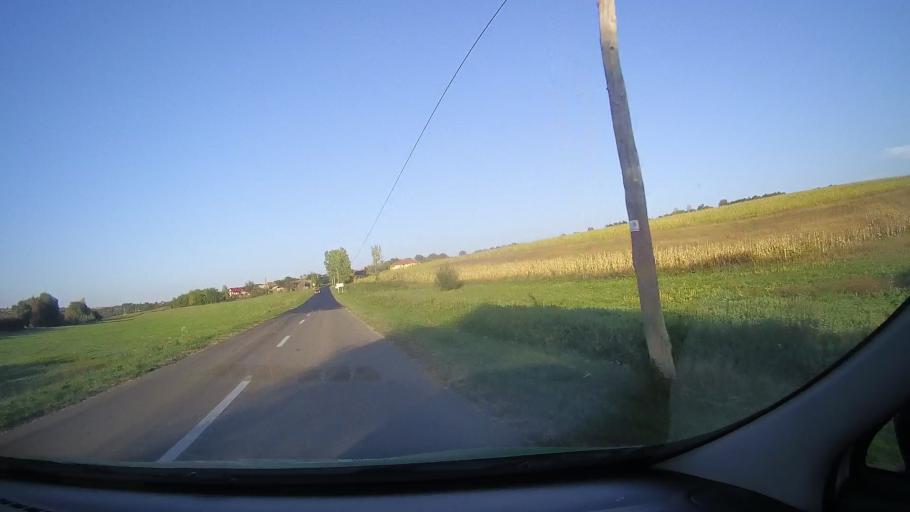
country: RO
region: Bihor
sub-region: Comuna Cetariu
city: Cetariu
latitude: 47.1325
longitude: 21.9856
